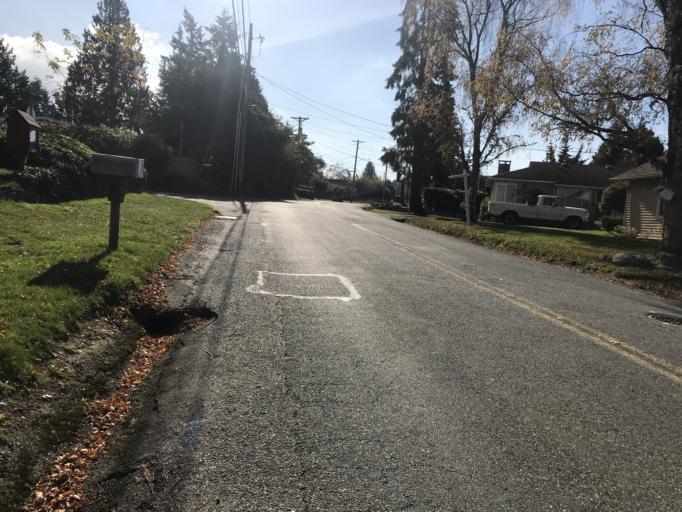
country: US
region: Washington
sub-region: Pierce County
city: University Place
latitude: 47.2454
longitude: -122.5526
